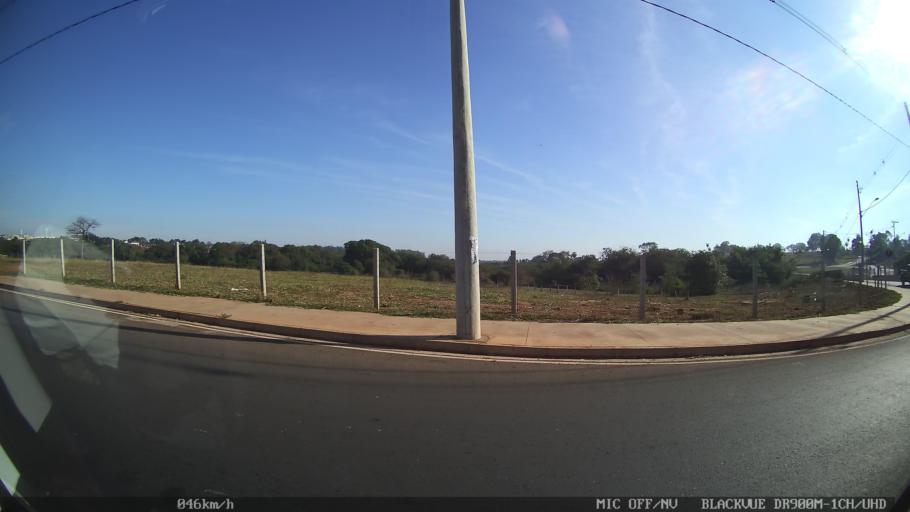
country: BR
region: Sao Paulo
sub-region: Sao Jose Do Rio Preto
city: Sao Jose do Rio Preto
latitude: -20.7601
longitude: -49.3712
